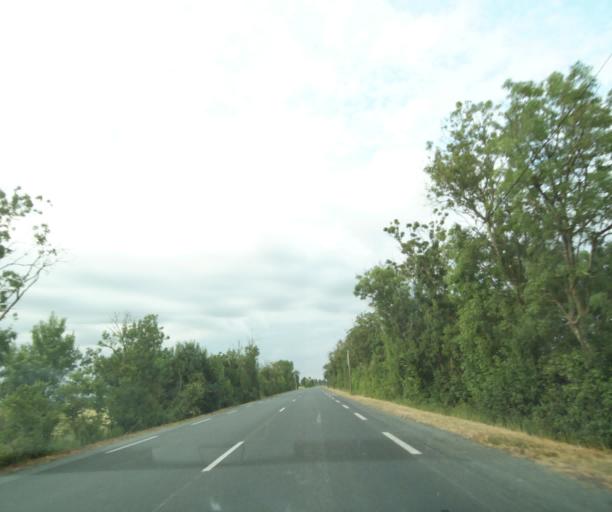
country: FR
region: Poitou-Charentes
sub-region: Departement de la Charente-Maritime
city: Marans
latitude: 46.3553
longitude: -0.9931
